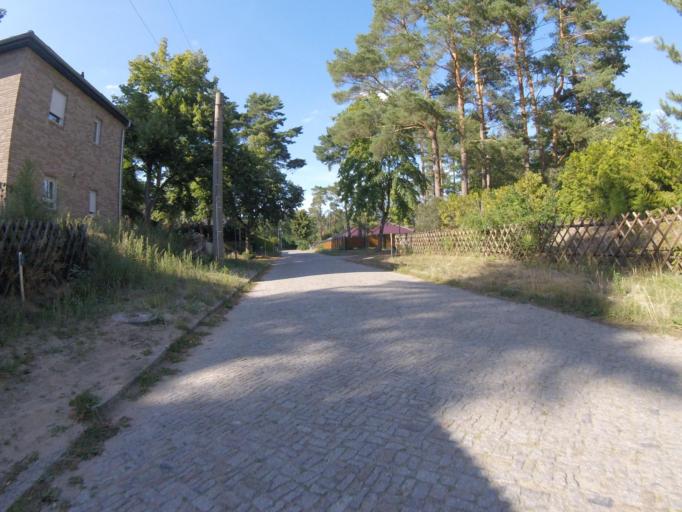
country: DE
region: Brandenburg
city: Wildau
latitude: 52.3120
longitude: 13.6973
